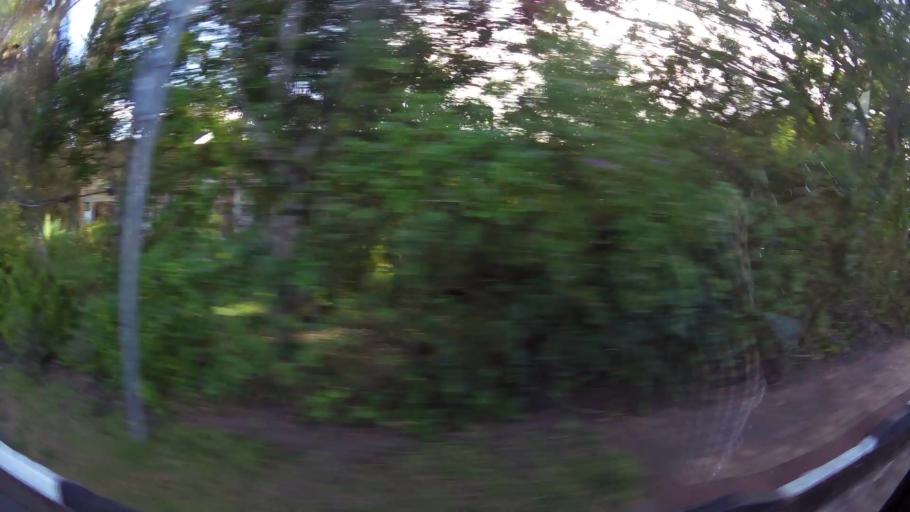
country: ZA
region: Western Cape
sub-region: Eden District Municipality
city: George
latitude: -33.9607
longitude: 22.4890
